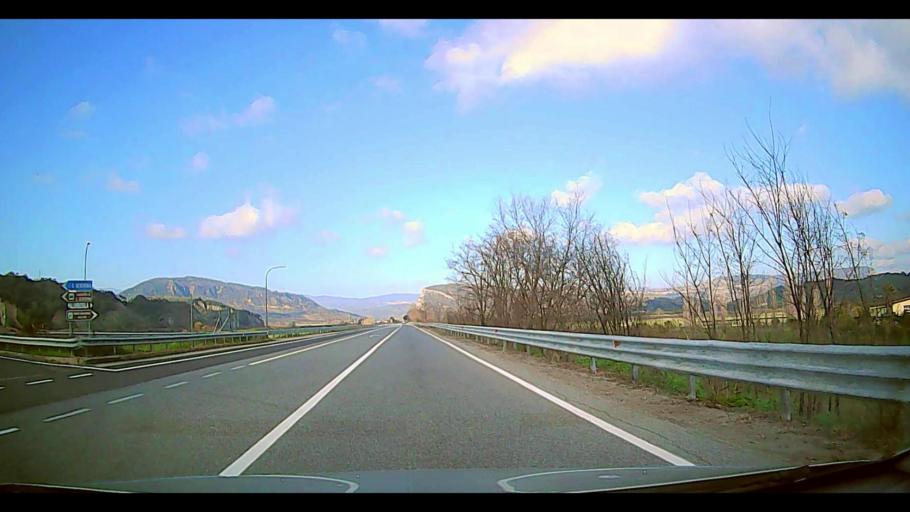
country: IT
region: Calabria
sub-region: Provincia di Crotone
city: Santa Severina
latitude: 39.1752
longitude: 16.9325
